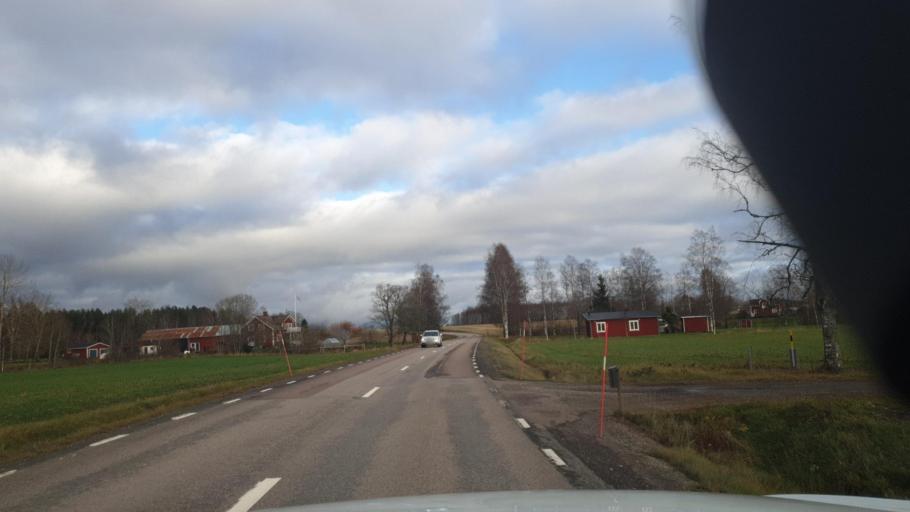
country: SE
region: Vaermland
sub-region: Sunne Kommun
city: Sunne
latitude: 59.7285
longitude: 13.1235
